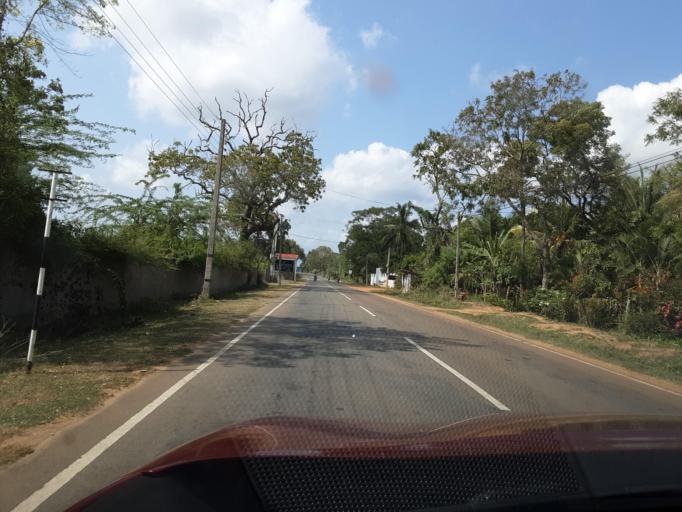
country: LK
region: Southern
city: Tangalla
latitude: 6.2770
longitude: 81.2293
